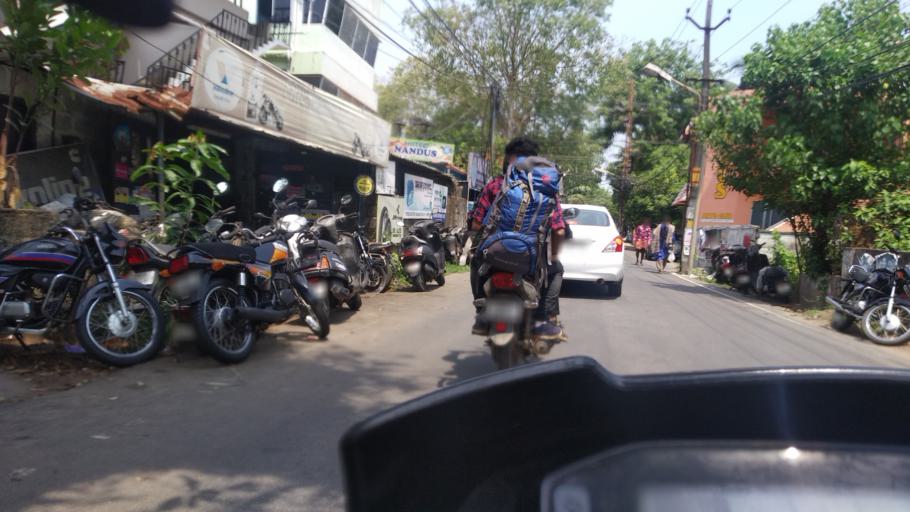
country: IN
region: Kerala
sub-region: Ernakulam
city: Cochin
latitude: 9.9602
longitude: 76.3013
